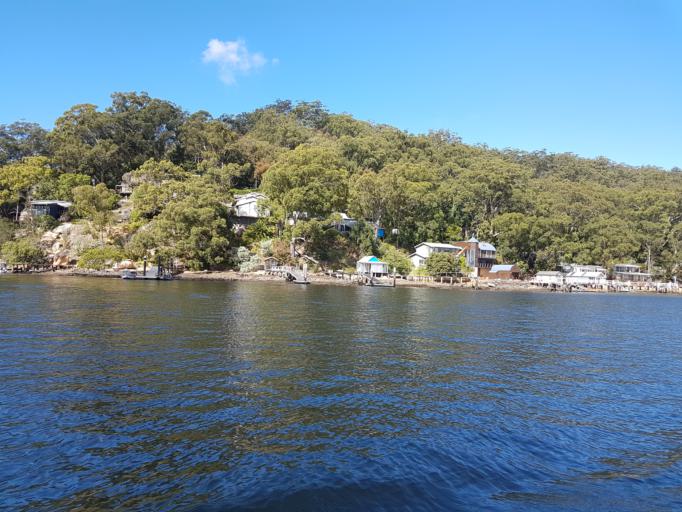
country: AU
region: New South Wales
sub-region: Gosford Shire
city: Umina
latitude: -33.5370
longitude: 151.2351
